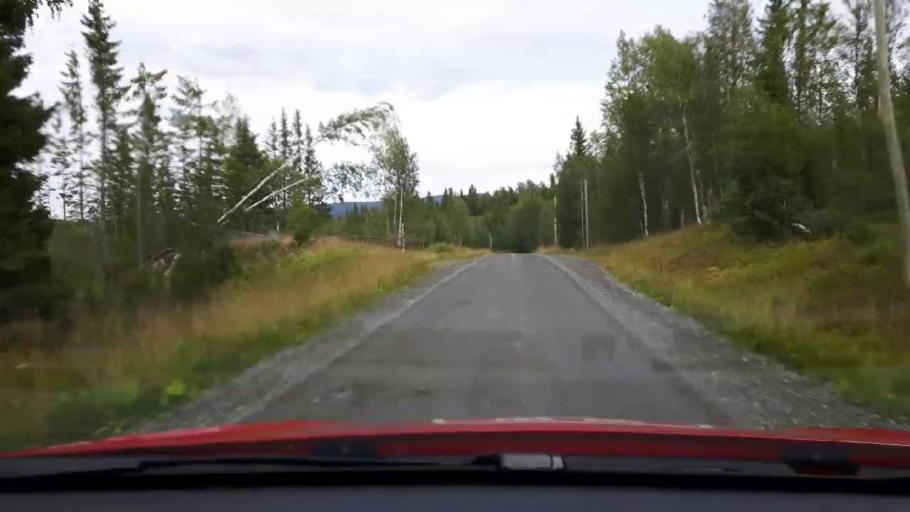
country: SE
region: Jaemtland
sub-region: Are Kommun
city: Are
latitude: 63.7640
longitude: 13.0924
